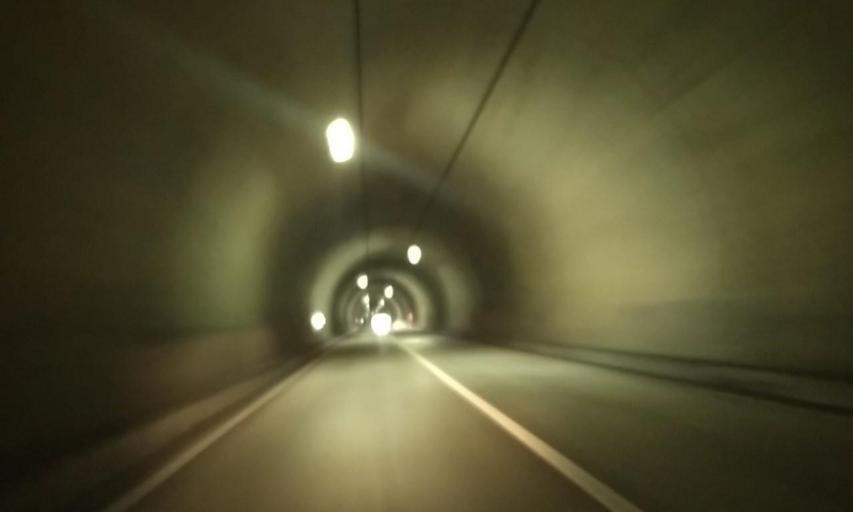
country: JP
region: Wakayama
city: Shingu
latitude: 33.8820
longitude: 135.8779
